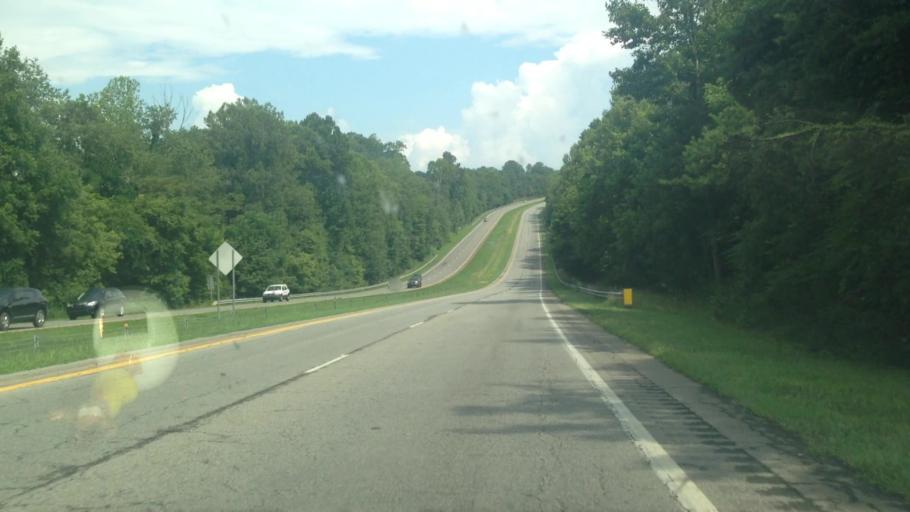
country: US
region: North Carolina
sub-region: Surry County
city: Flat Rock
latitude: 36.4679
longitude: -80.5703
